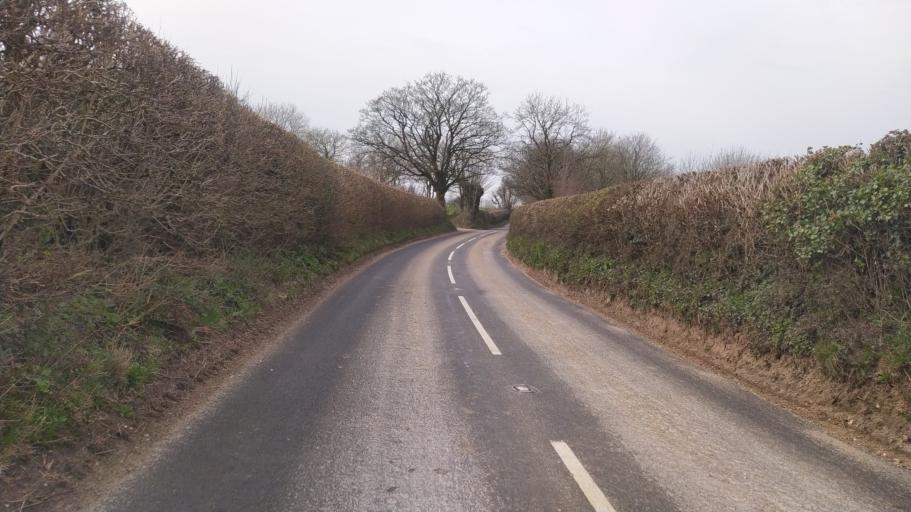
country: GB
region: England
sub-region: Dorset
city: Beaminster
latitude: 50.8072
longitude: -2.6994
